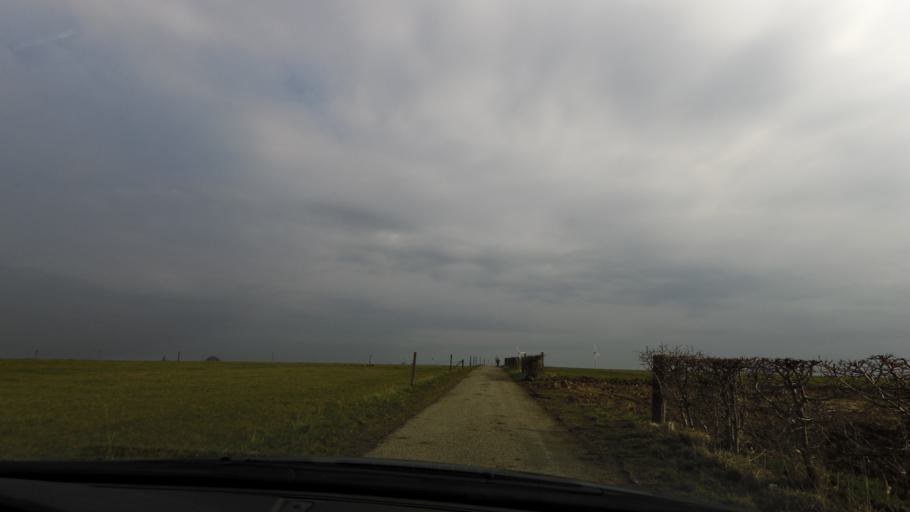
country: NL
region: Limburg
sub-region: Gemeente Simpelveld
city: Simpelveld
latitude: 50.8088
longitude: 6.0081
